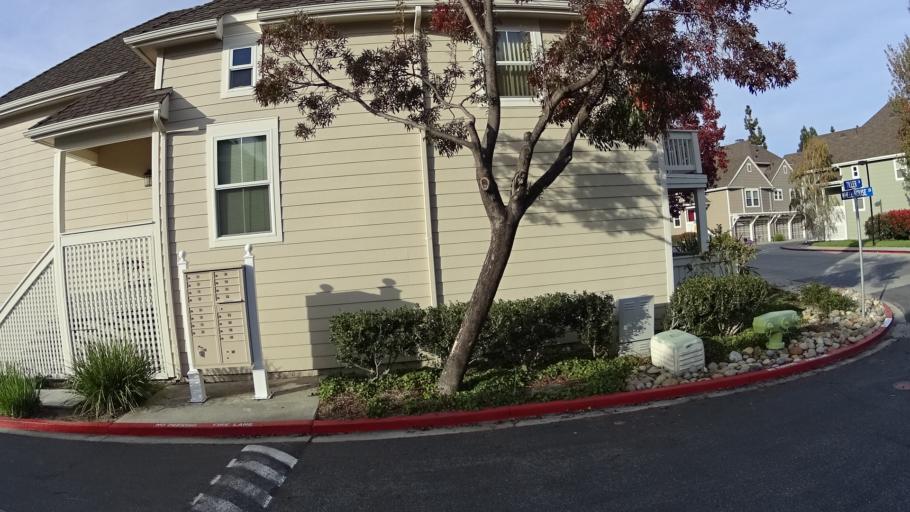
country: US
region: California
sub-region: San Mateo County
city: Redwood Shores
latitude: 37.5479
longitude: -122.2547
